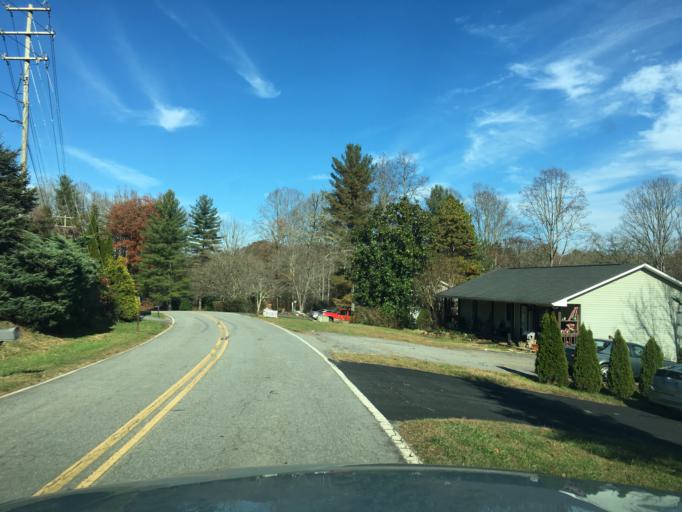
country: US
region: North Carolina
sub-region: Henderson County
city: Etowah
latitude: 35.3170
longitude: -82.6187
